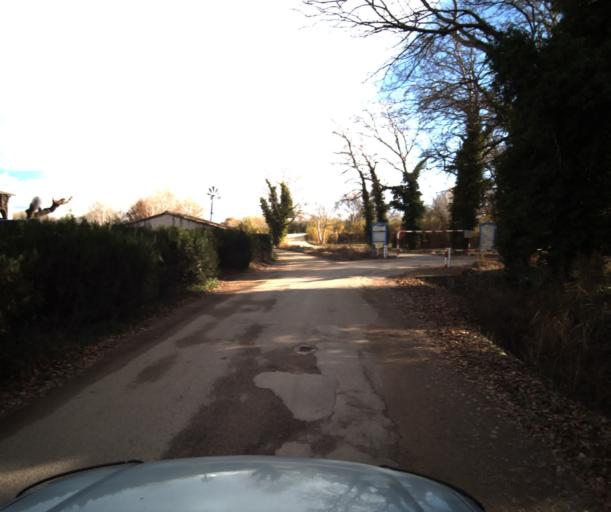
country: FR
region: Provence-Alpes-Cote d'Azur
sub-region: Departement du Vaucluse
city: Pertuis
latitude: 43.6705
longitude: 5.4985
